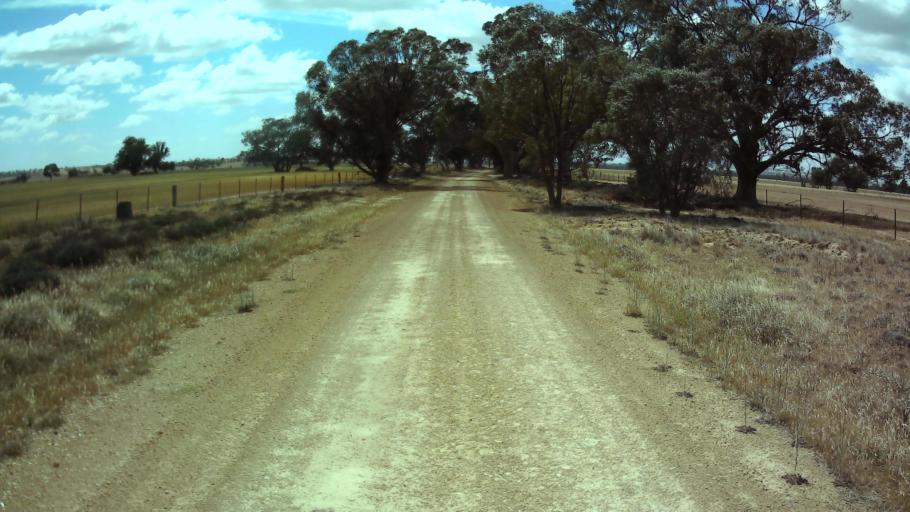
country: AU
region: New South Wales
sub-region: Weddin
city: Grenfell
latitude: -33.9979
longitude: 148.2954
